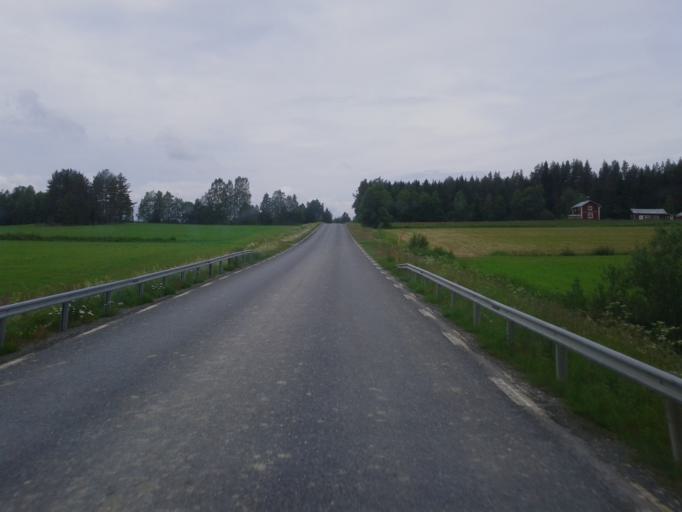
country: SE
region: Vaesterbotten
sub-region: Skelleftea Kommun
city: Viken
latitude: 64.8922
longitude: 20.7221
